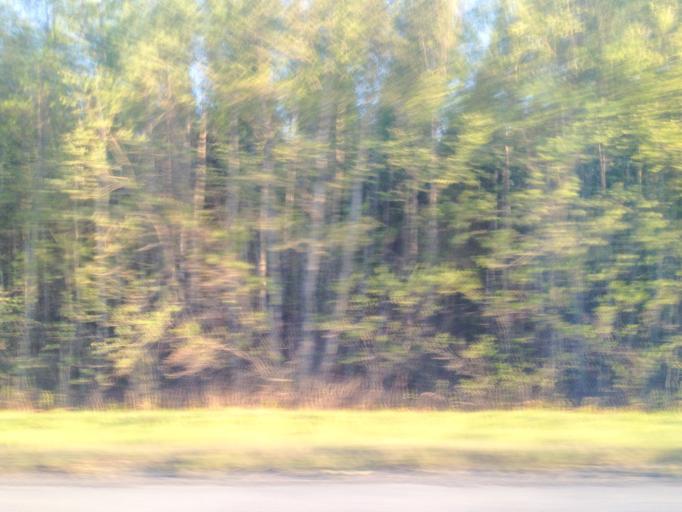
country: FI
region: Haeme
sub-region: Haemeenlinna
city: Parola
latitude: 61.0677
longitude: 24.3112
